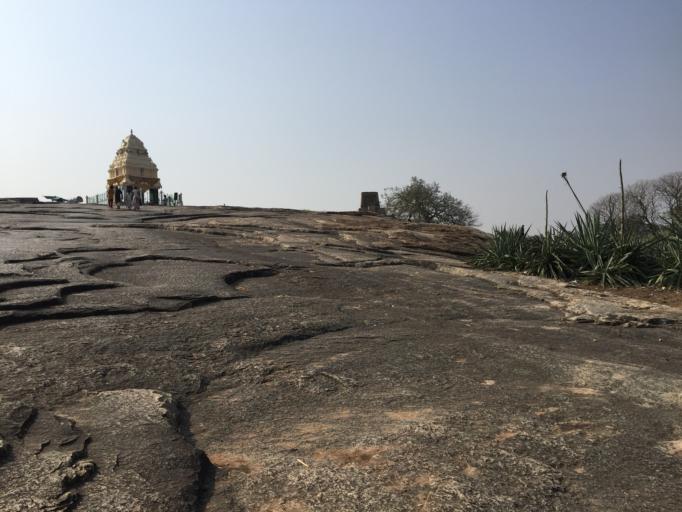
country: IN
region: Karnataka
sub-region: Bangalore Urban
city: Bangalore
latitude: 12.9490
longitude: 77.5890
